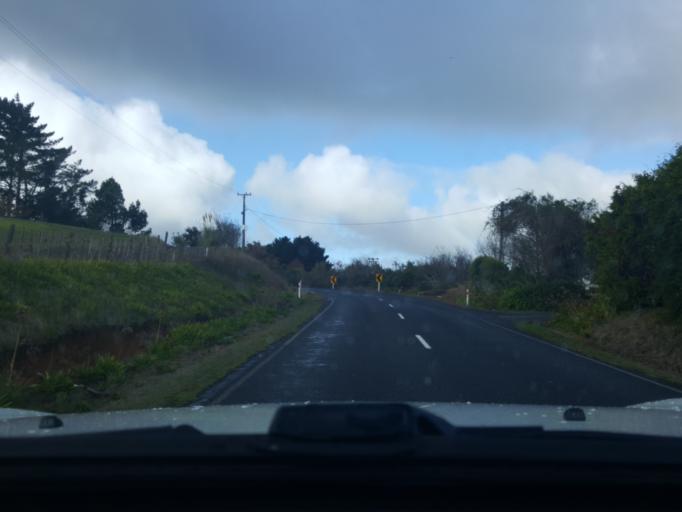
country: NZ
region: Waikato
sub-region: Waikato District
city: Te Kauwhata
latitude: -37.4438
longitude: 175.0808
